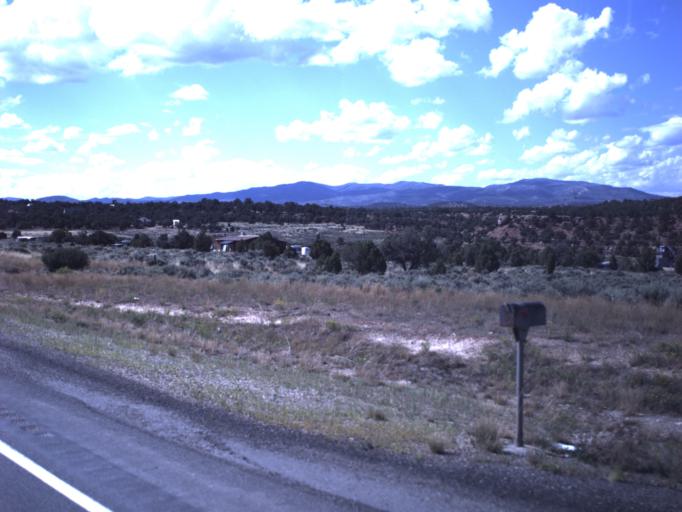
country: US
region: Utah
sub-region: Duchesne County
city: Duchesne
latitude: 40.2065
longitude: -110.8108
